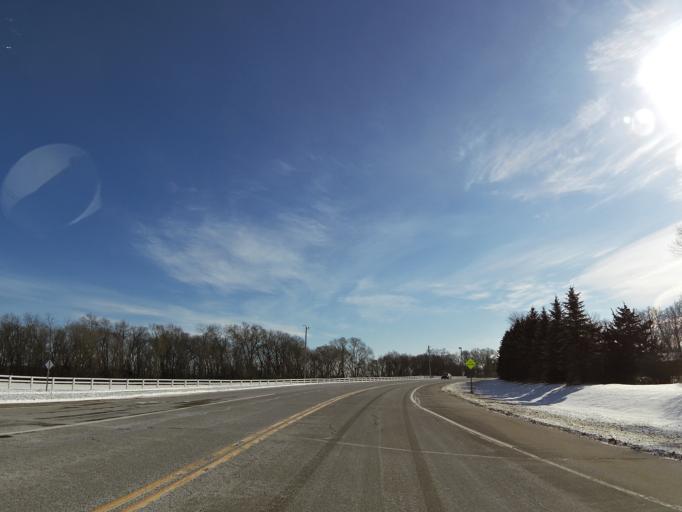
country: US
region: Minnesota
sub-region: Dakota County
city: Hastings
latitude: 44.7564
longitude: -92.8867
